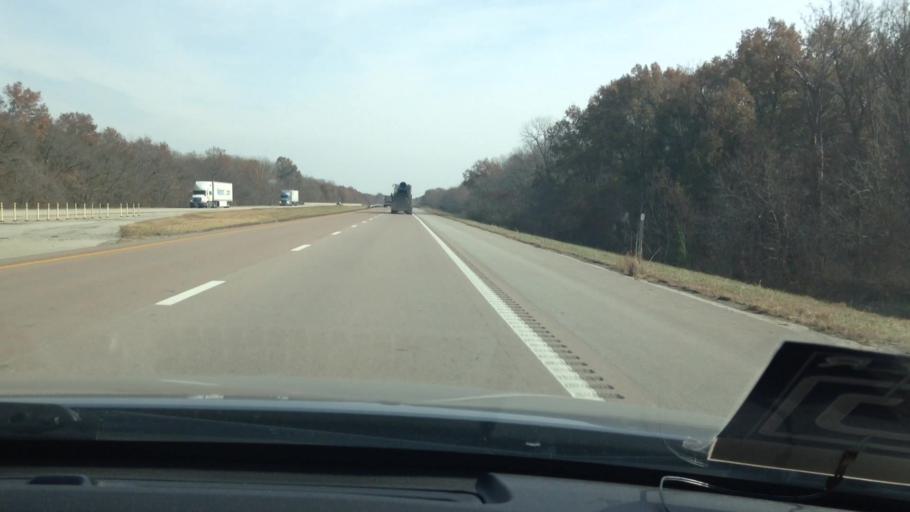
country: US
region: Missouri
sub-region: Henry County
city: Clinton
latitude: 38.4277
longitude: -93.9056
